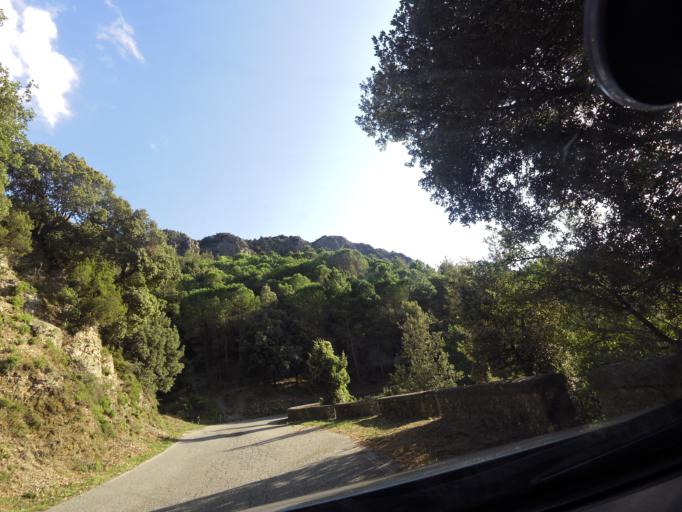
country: IT
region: Calabria
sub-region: Provincia di Reggio Calabria
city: Pazzano
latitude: 38.4644
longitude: 16.4284
